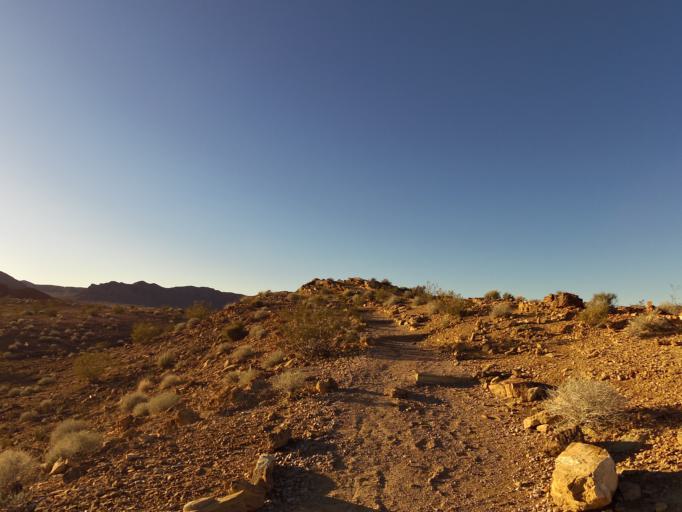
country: US
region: Nevada
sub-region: Clark County
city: Moapa Valley
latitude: 36.4221
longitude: -114.5404
